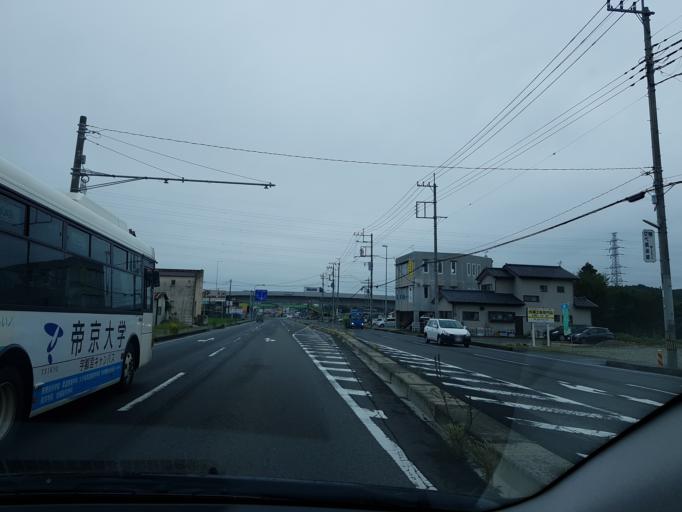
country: JP
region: Tochigi
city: Utsunomiya-shi
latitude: 36.5956
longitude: 139.8962
